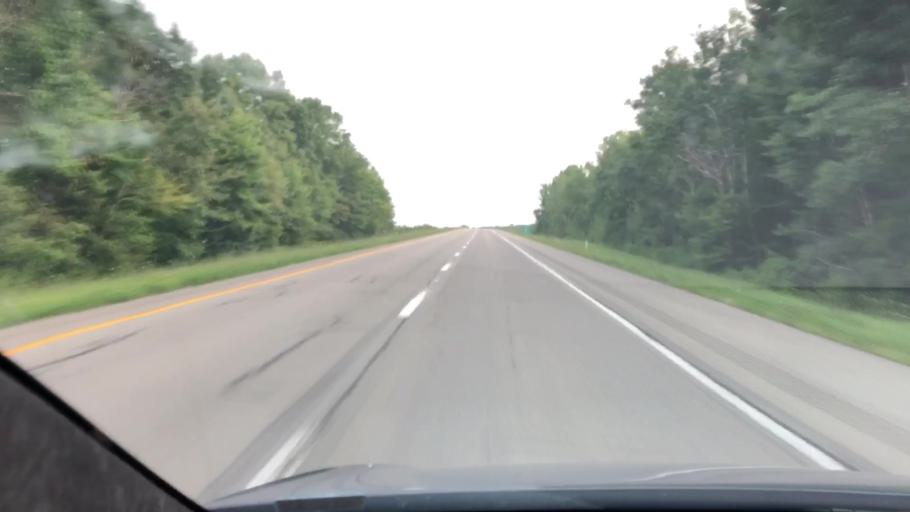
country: US
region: Pennsylvania
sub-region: Venango County
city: Franklin
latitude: 41.2741
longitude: -79.9183
